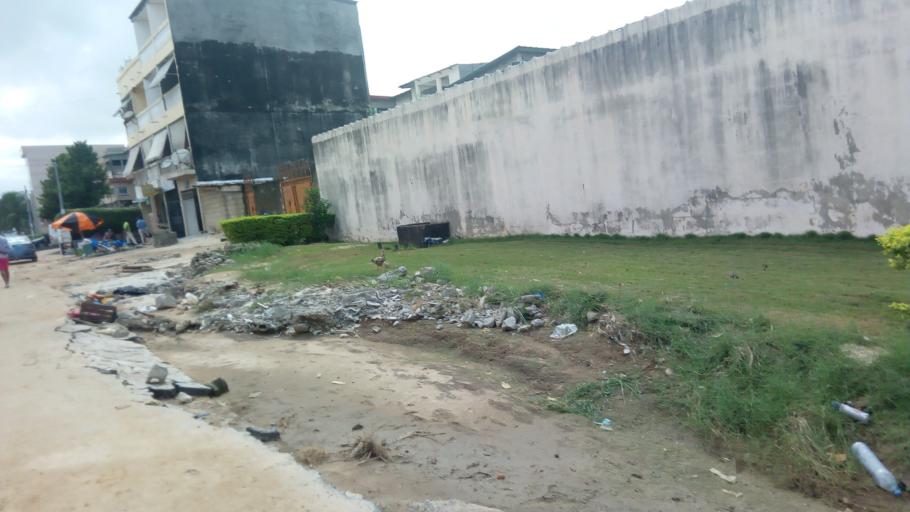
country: CI
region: Lagunes
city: Bingerville
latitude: 5.3663
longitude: -3.9590
